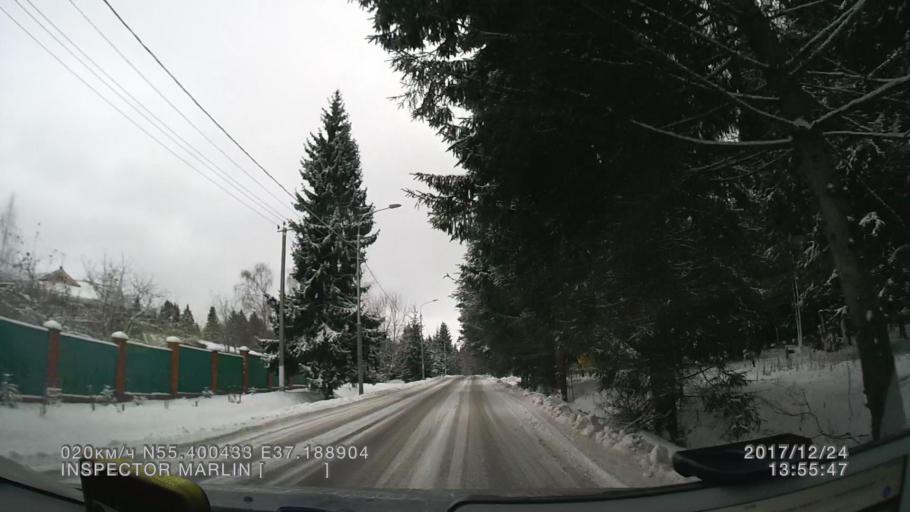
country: RU
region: Moskovskaya
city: Troitsk
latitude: 55.4004
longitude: 37.1889
